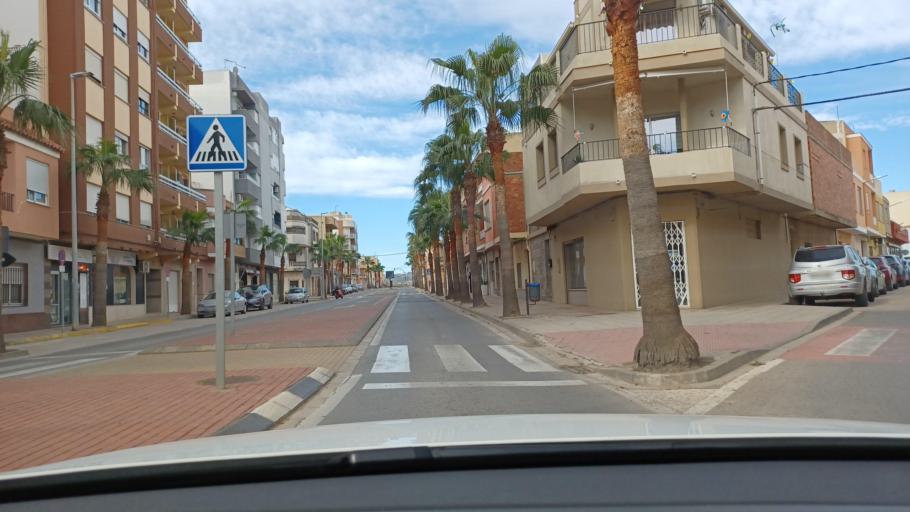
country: ES
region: Valencia
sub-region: Provincia de Valencia
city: Benifaio
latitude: 39.2886
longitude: -0.4247
